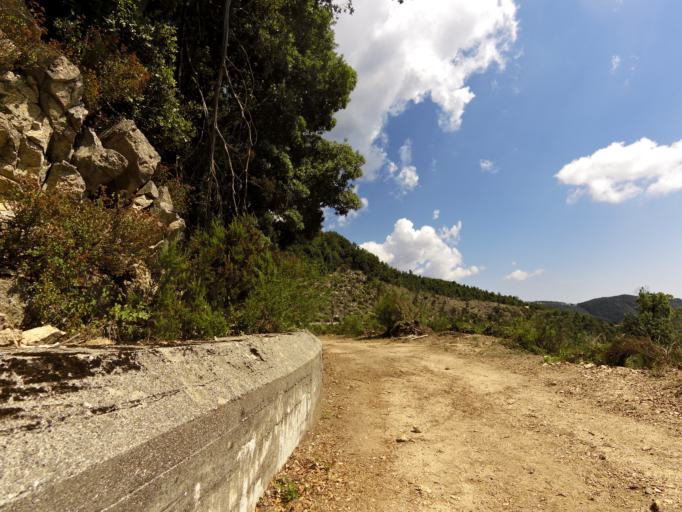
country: IT
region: Calabria
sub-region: Provincia di Vibo-Valentia
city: Nardodipace
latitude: 38.5067
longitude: 16.3918
